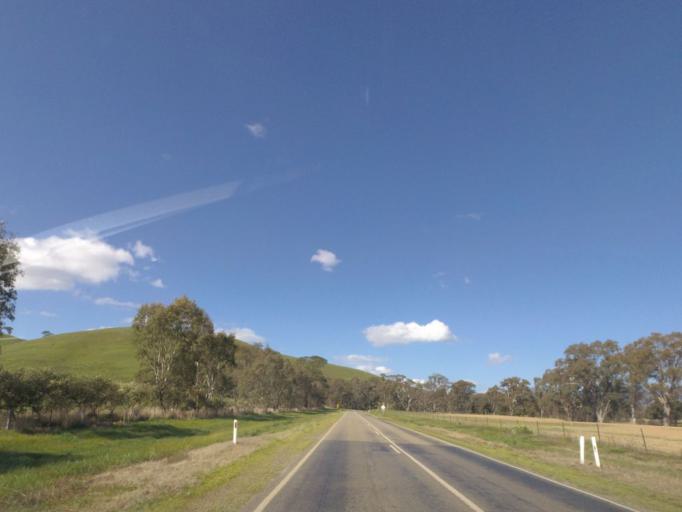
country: AU
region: Victoria
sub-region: Murrindindi
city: Alexandra
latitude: -37.2286
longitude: 145.7593
